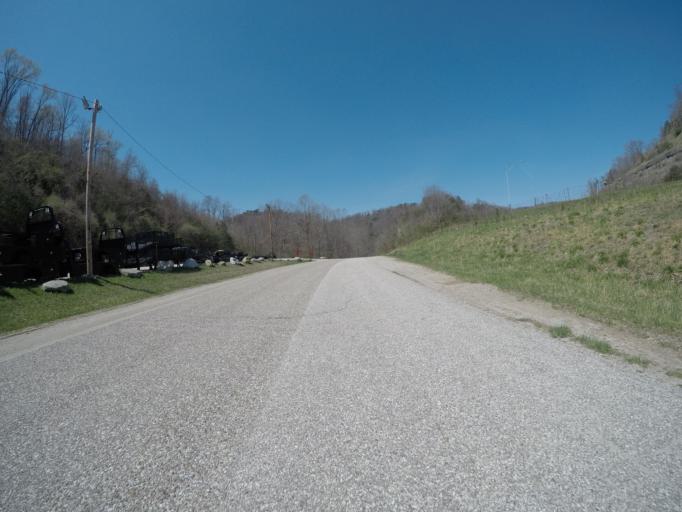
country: US
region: West Virginia
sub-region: Kanawha County
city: Charleston
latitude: 38.3947
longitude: -81.5926
